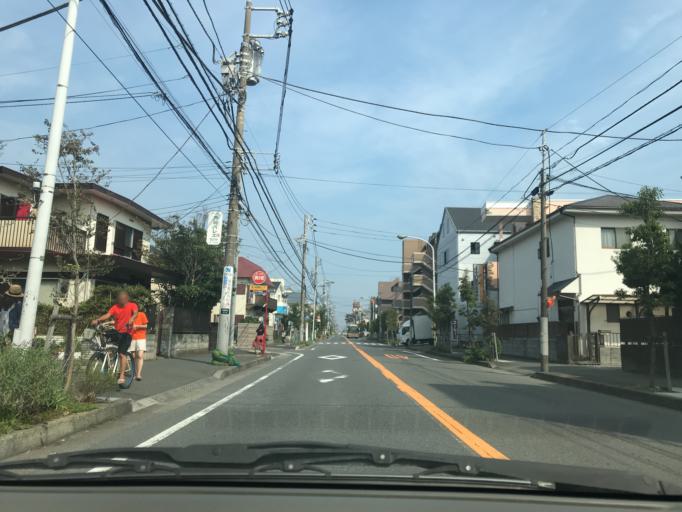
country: JP
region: Kanagawa
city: Chigasaki
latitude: 35.3248
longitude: 139.4091
